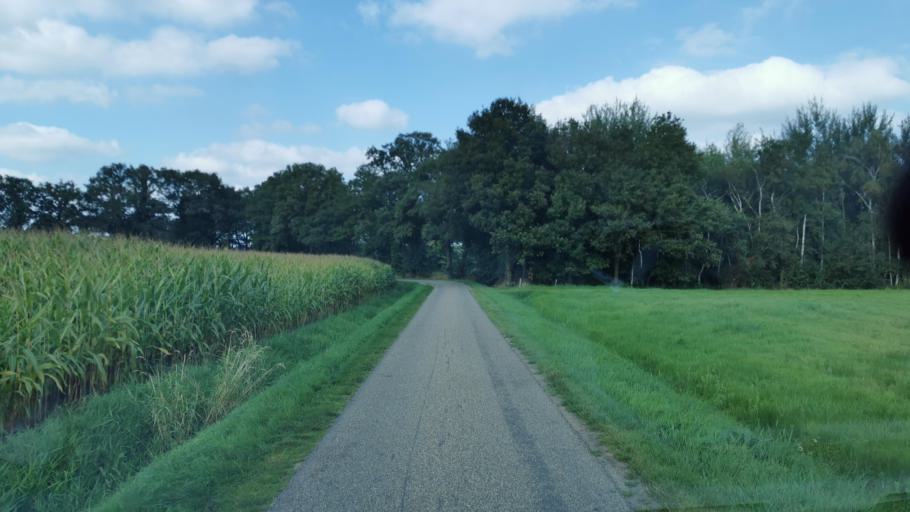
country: NL
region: Overijssel
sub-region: Gemeente Hengelo
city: Hengelo
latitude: 52.3200
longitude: 6.8139
